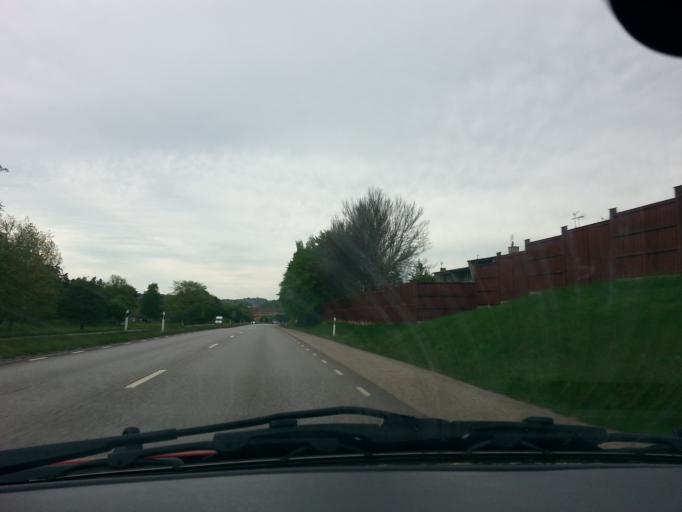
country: SE
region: Vaestra Goetaland
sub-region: Alingsas Kommun
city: Alingsas
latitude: 57.9203
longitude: 12.5224
